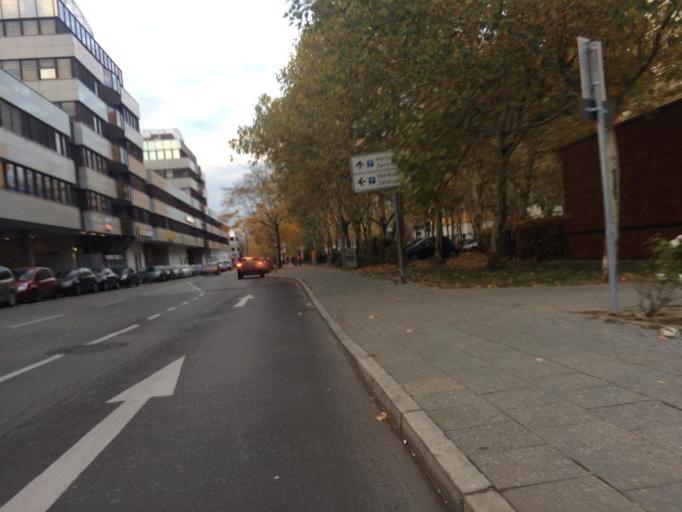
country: DE
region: Berlin
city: Markisches Viertel
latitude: 52.5971
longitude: 13.3563
